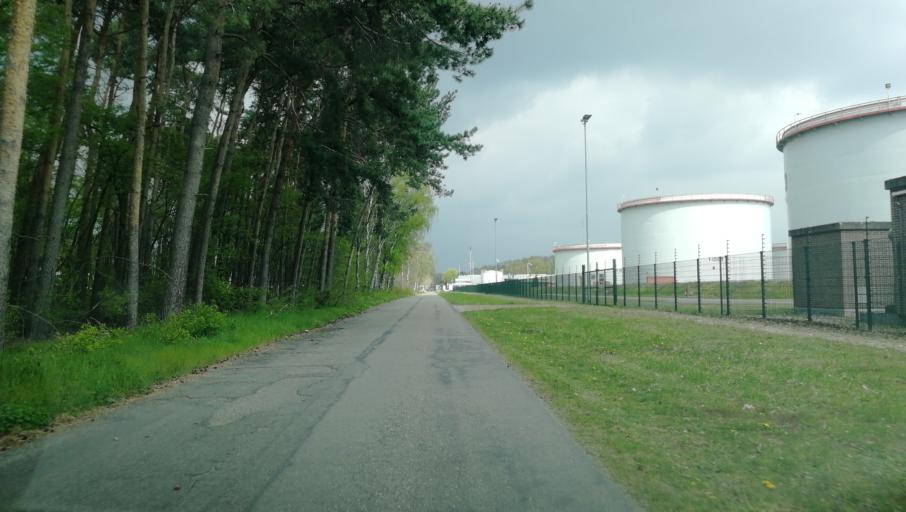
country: NL
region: Limburg
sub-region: Gemeente Venlo
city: Venlo
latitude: 51.3758
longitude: 6.2163
